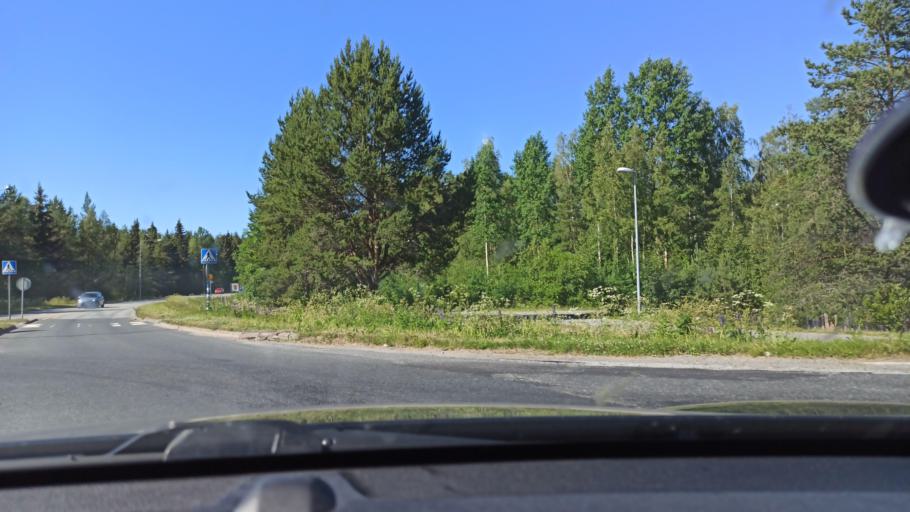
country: FI
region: Ostrobothnia
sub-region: Jakobstadsregionen
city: Jakobstad
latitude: 63.6544
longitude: 22.7148
